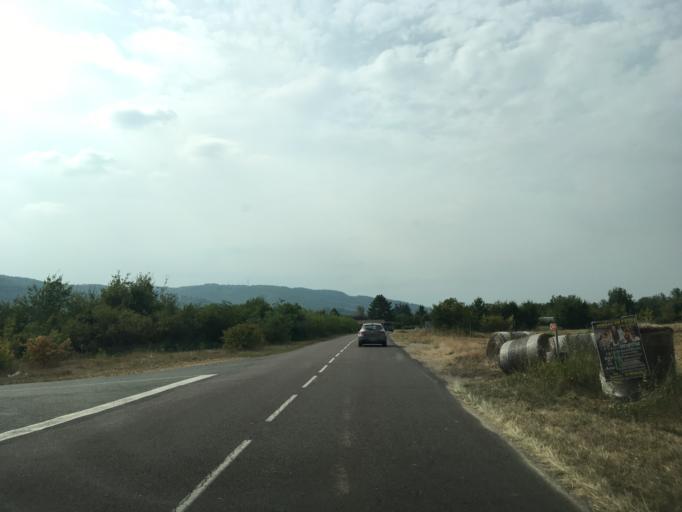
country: FR
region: Midi-Pyrenees
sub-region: Departement du Lot
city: Souillac
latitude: 44.8588
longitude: 1.5026
